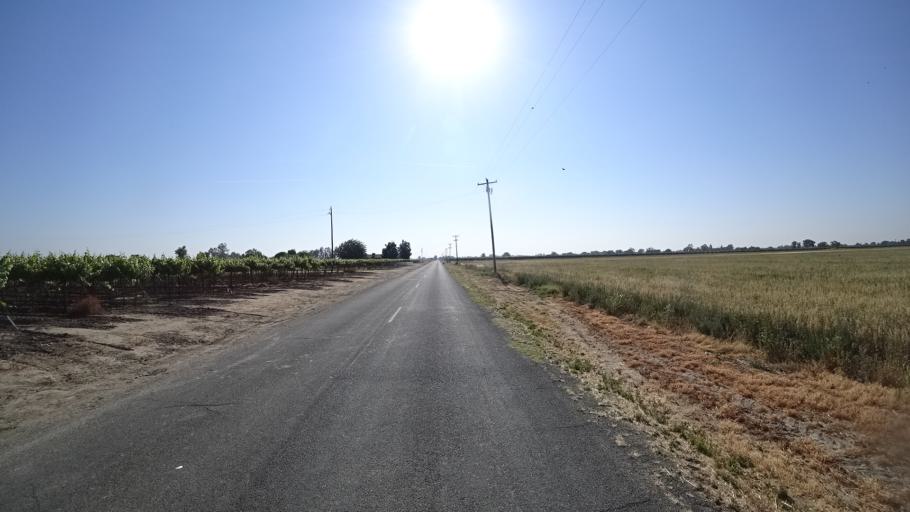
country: US
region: California
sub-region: Fresno County
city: Riverdale
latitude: 36.3657
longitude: -119.8679
